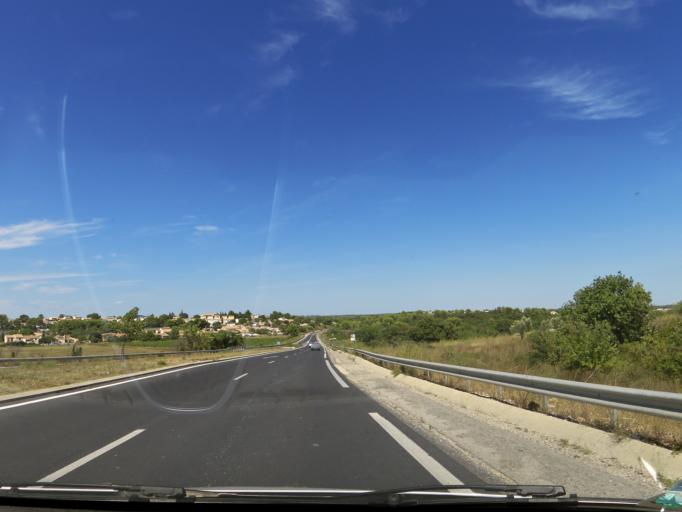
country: FR
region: Languedoc-Roussillon
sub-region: Departement de l'Herault
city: Jacou
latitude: 43.6536
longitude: 3.9223
